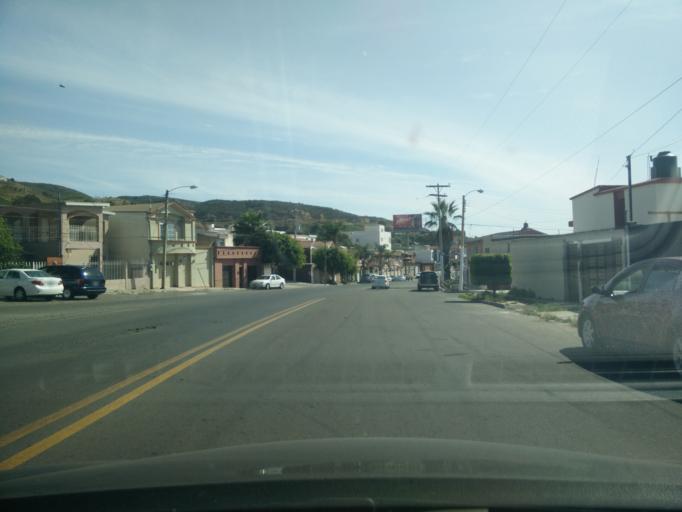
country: MX
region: Baja California
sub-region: Tijuana
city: La Esperanza [Granjas Familiares]
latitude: 32.5123
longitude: -117.1123
